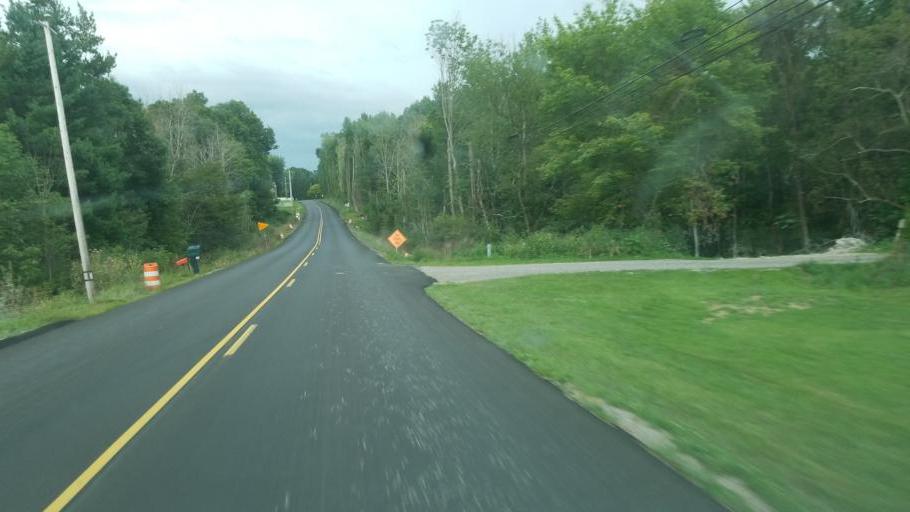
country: US
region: Pennsylvania
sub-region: Clarion County
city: Knox
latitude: 41.2521
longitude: -79.5483
